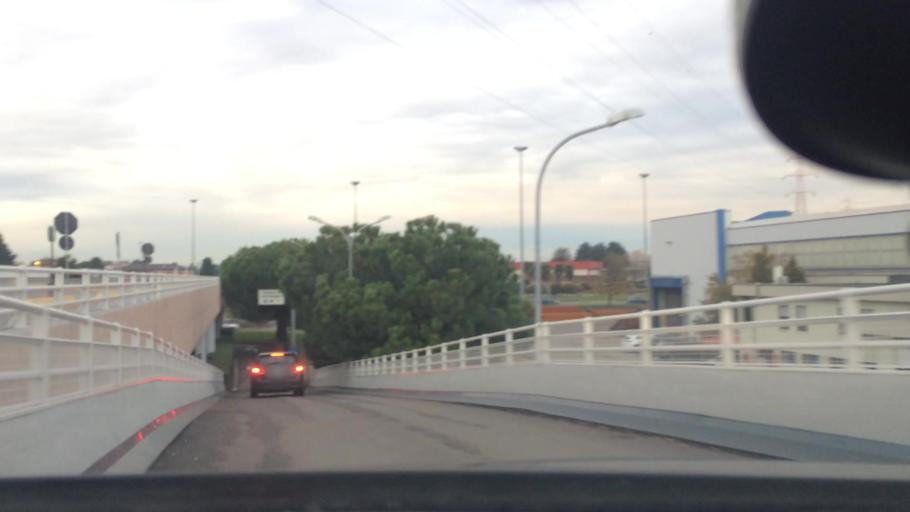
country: IT
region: Lombardy
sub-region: Citta metropolitana di Milano
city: Rescaldina
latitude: 45.6102
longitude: 8.9653
